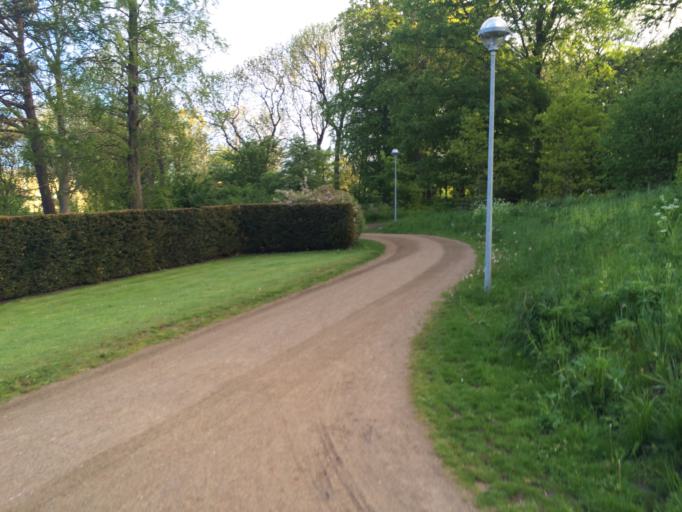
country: DK
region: North Denmark
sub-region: Alborg Kommune
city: Aalborg
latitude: 57.0318
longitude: 9.9468
